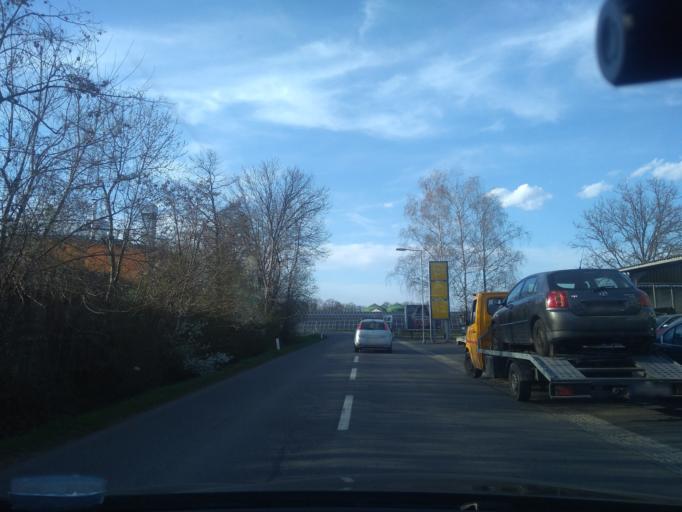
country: AT
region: Styria
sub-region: Politischer Bezirk Suedoststeiermark
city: Mureck
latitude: 46.7130
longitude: 15.7687
